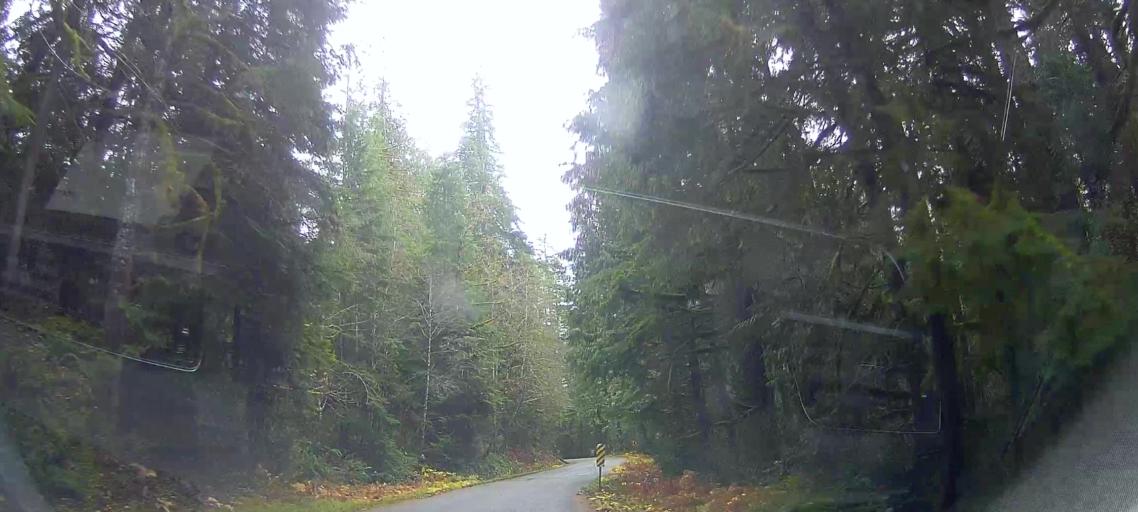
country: US
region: Washington
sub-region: Snohomish County
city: Darrington
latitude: 48.5242
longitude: -121.3846
